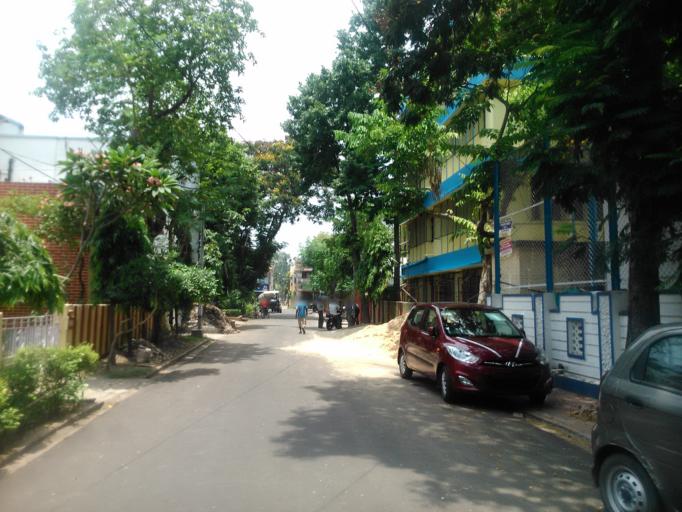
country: IN
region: West Bengal
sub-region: North 24 Parganas
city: Garui
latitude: 22.5946
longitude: 88.4078
